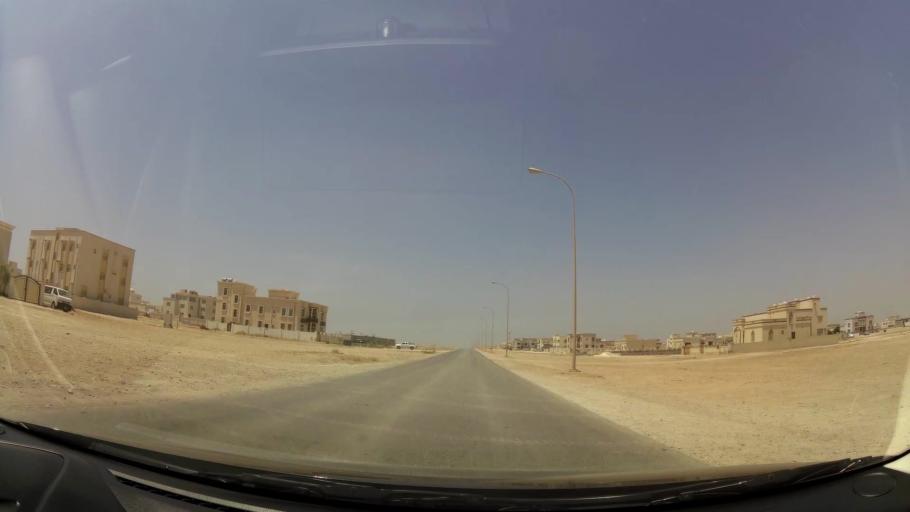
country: OM
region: Zufar
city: Salalah
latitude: 17.0886
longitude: 54.2051
